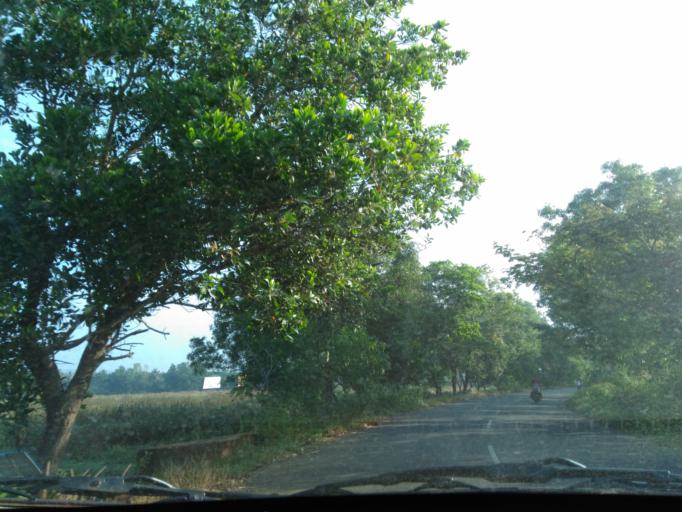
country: IN
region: Goa
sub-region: South Goa
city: Chinchinim
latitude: 15.2179
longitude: 73.9762
